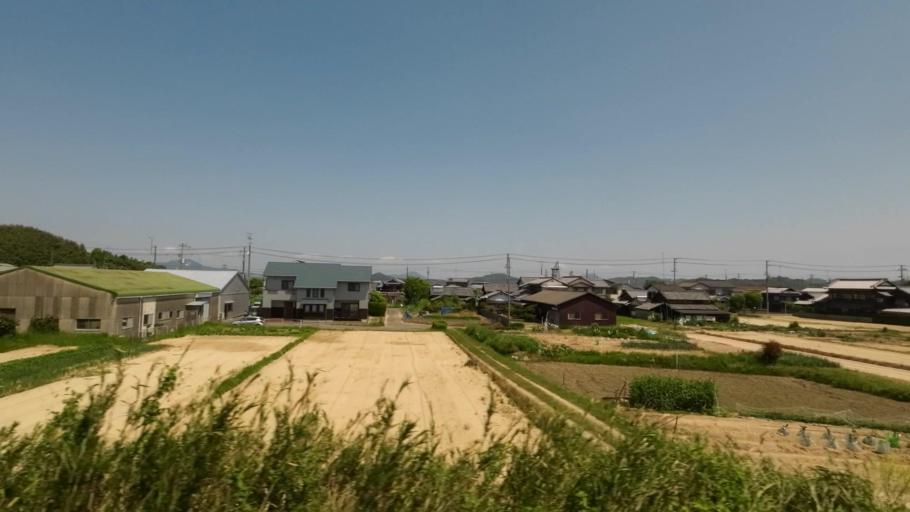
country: JP
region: Ehime
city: Hojo
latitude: 34.0622
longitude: 132.9029
